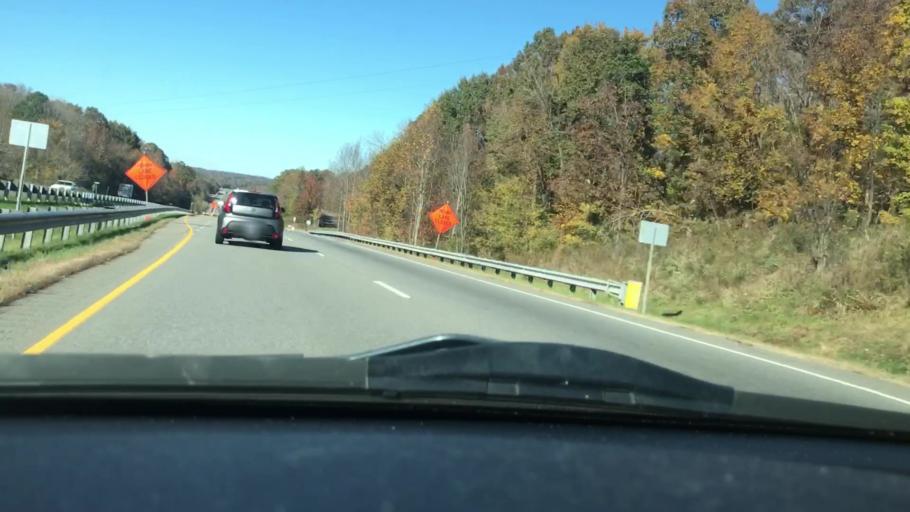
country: US
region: North Carolina
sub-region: Rockingham County
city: Mayodan
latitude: 36.4306
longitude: -79.9296
